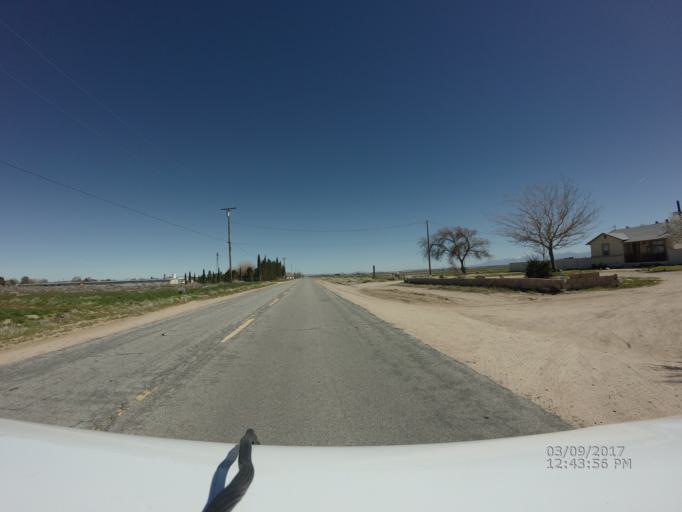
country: US
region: California
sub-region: Los Angeles County
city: Quartz Hill
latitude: 34.7474
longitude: -118.2854
